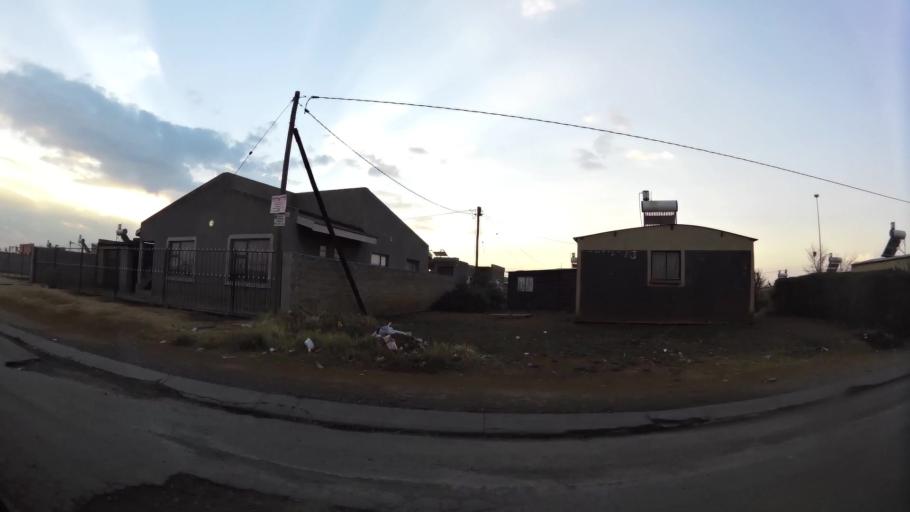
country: ZA
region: Gauteng
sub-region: City of Johannesburg Metropolitan Municipality
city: Orange Farm
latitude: -26.5626
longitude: 27.8366
